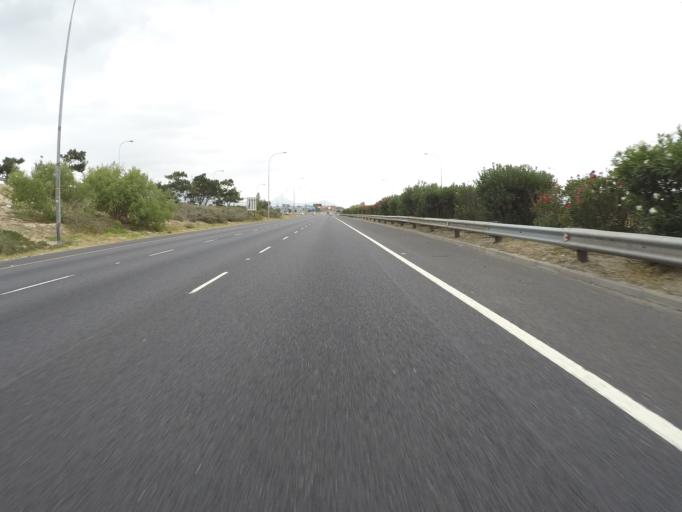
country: ZA
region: Western Cape
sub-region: City of Cape Town
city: Sunset Beach
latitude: -33.8903
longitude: 18.5526
